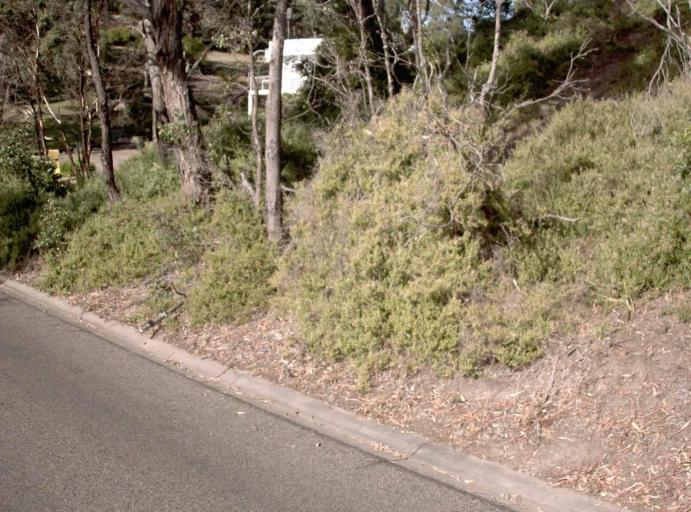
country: AU
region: Victoria
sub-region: East Gippsland
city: Lakes Entrance
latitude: -37.8845
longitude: 147.8599
